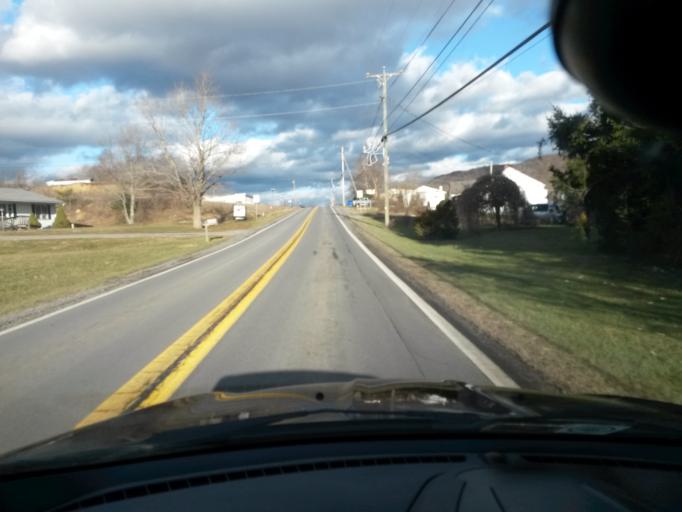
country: US
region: Virginia
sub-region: Giles County
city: Pembroke
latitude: 37.4490
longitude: -80.6764
